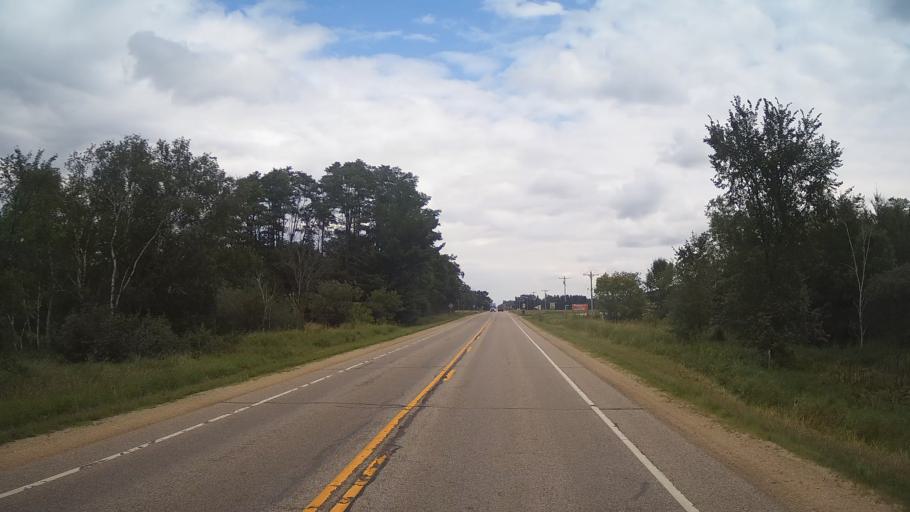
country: US
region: Wisconsin
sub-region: Waushara County
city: Wautoma
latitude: 44.0684
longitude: -89.3591
